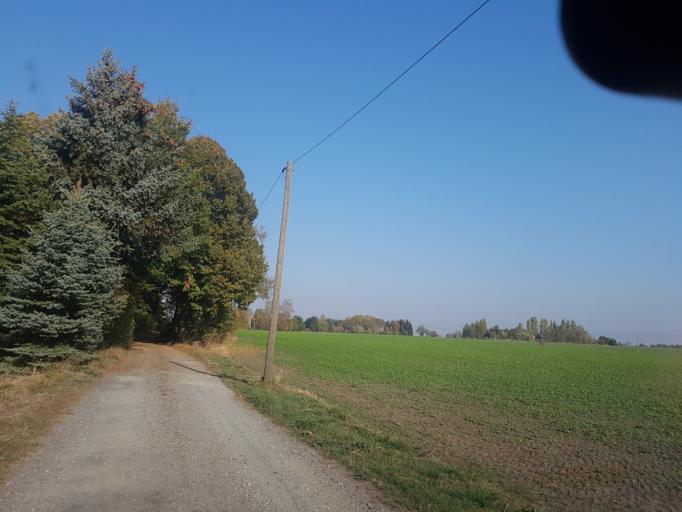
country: DE
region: Brandenburg
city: Finsterwalde
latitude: 51.6008
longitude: 13.7042
